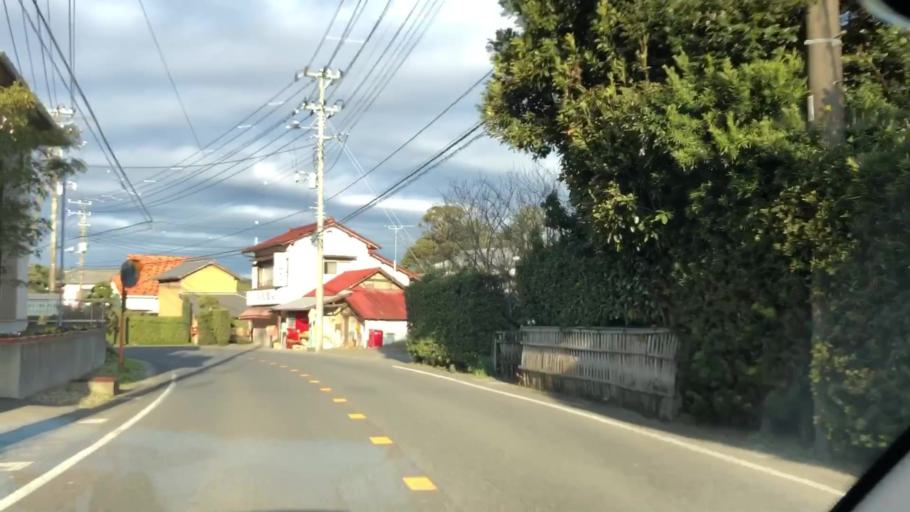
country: JP
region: Chiba
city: Tateyama
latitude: 34.9816
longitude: 139.9481
